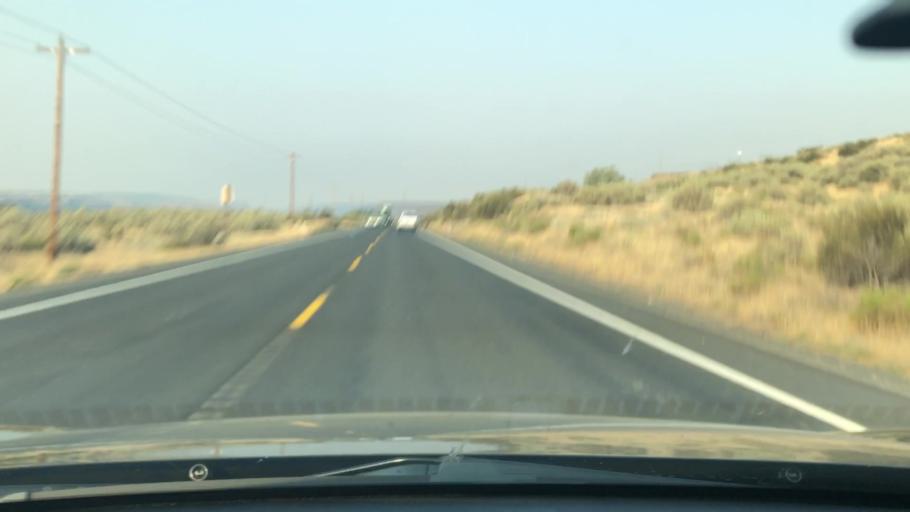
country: US
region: Oregon
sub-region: Umatilla County
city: Stanfield
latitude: 45.9186
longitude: -119.1272
